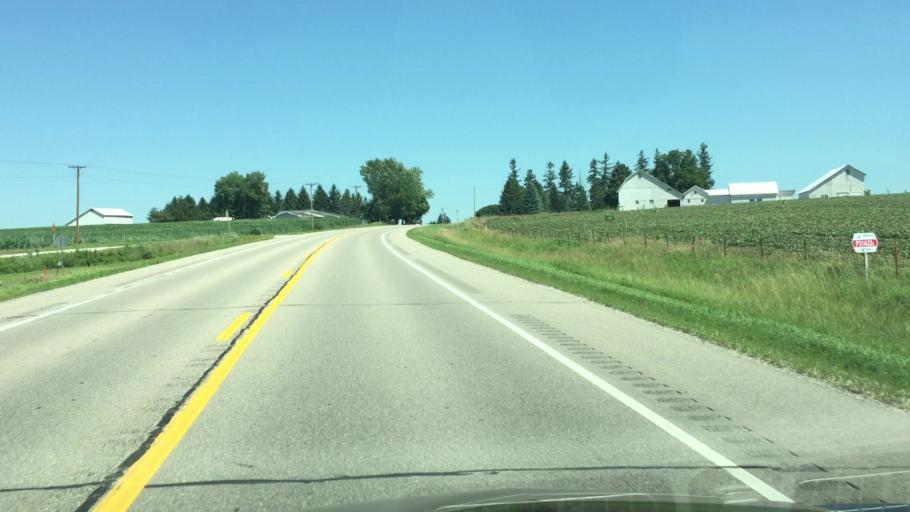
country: US
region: Iowa
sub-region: Johnson County
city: Solon
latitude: 41.8148
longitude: -91.4952
